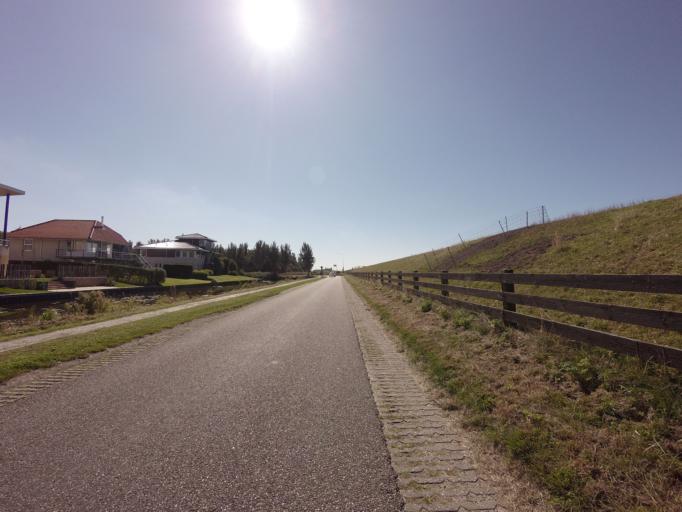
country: NL
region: Friesland
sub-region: Sudwest Fryslan
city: Koudum
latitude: 52.9378
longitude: 5.4026
